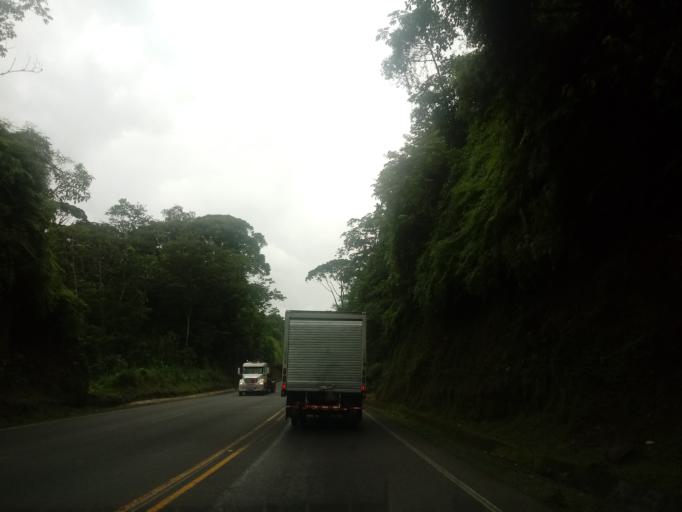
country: CR
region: San Jose
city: Dulce Nombre de Jesus
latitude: 10.1694
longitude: -83.9340
